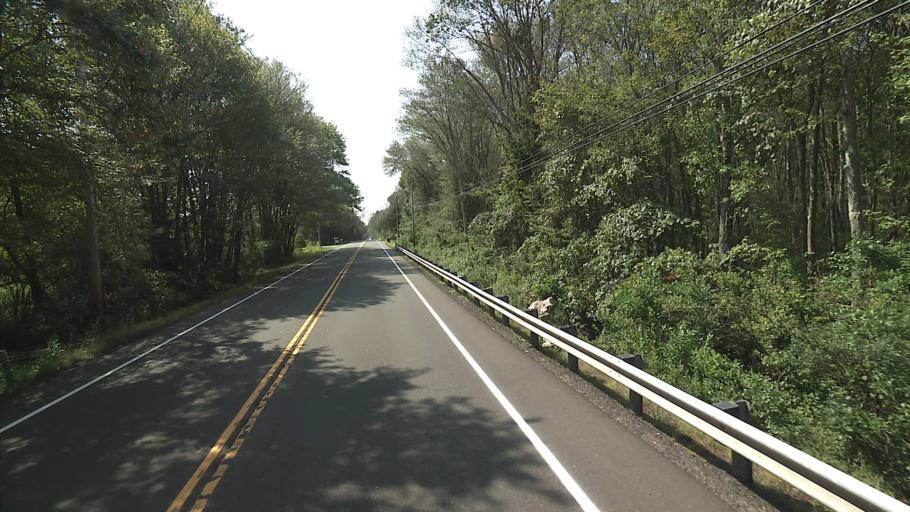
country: US
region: Connecticut
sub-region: Middlesex County
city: Durham
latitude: 41.4261
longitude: -72.6505
